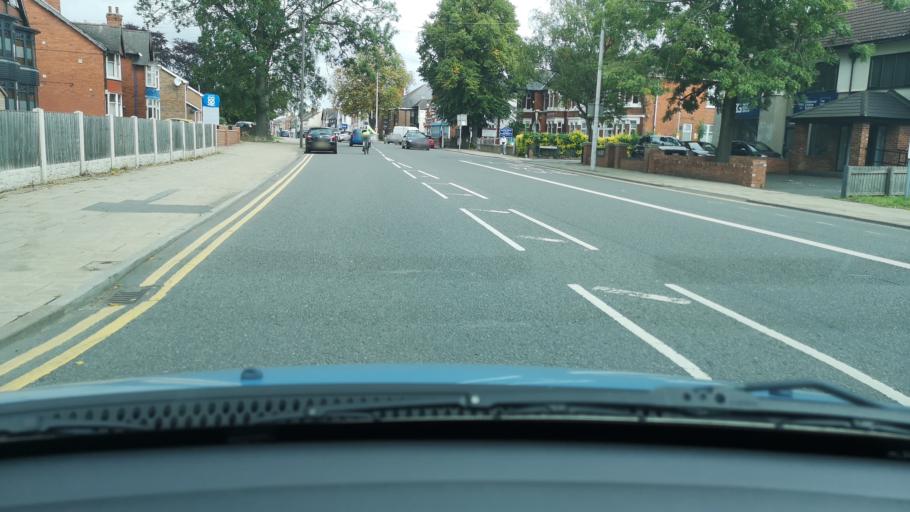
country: GB
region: England
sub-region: North Lincolnshire
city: Scunthorpe
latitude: 53.5873
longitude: -0.6539
